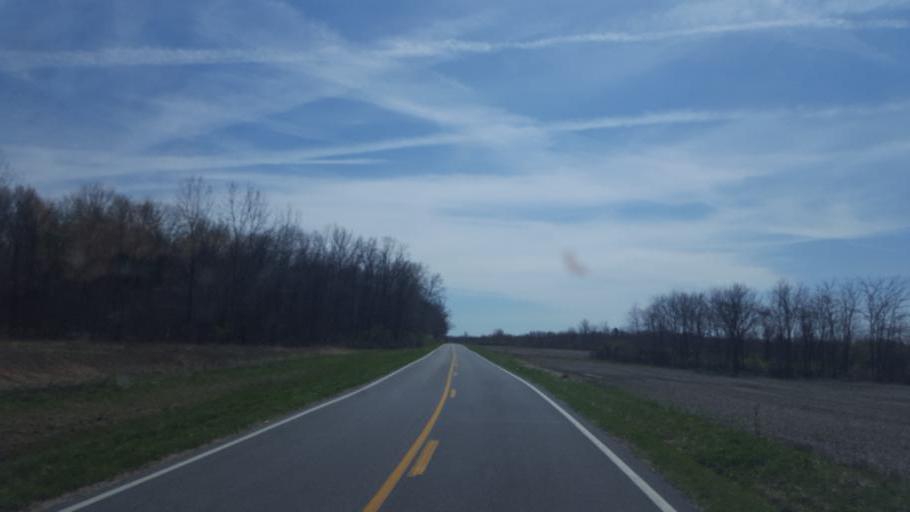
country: US
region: Ohio
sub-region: Delaware County
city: Ashley
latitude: 40.3970
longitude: -83.0386
